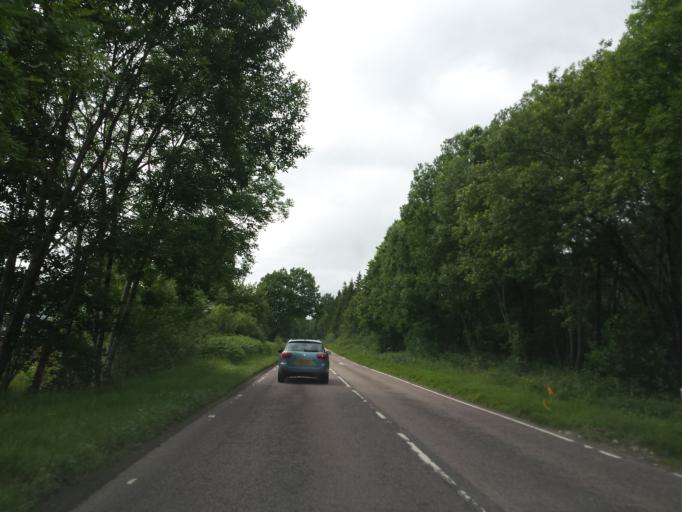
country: GB
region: Scotland
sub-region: Highland
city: Fort William
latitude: 56.8552
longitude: -5.2387
